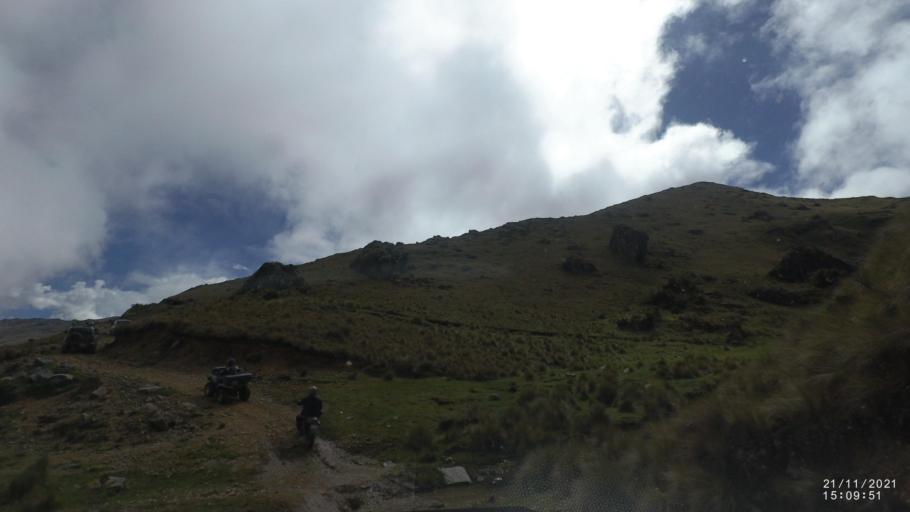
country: BO
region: Cochabamba
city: Cochabamba
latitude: -16.9554
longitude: -66.2612
